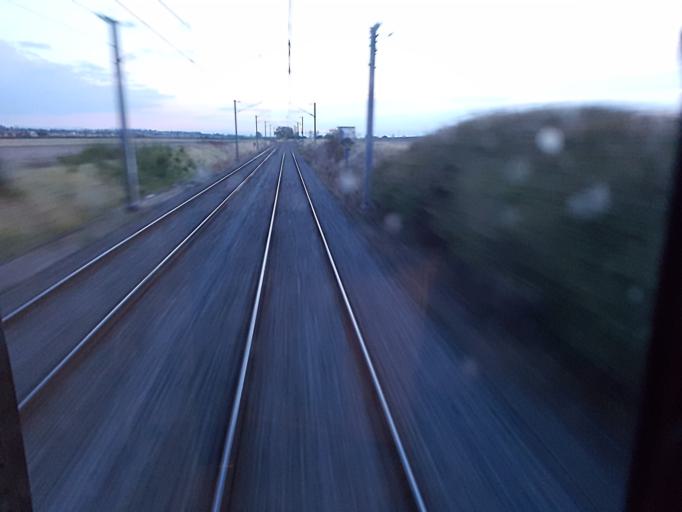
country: FR
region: Auvergne
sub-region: Departement du Puy-de-Dome
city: Randan
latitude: 45.9915
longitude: 3.3232
